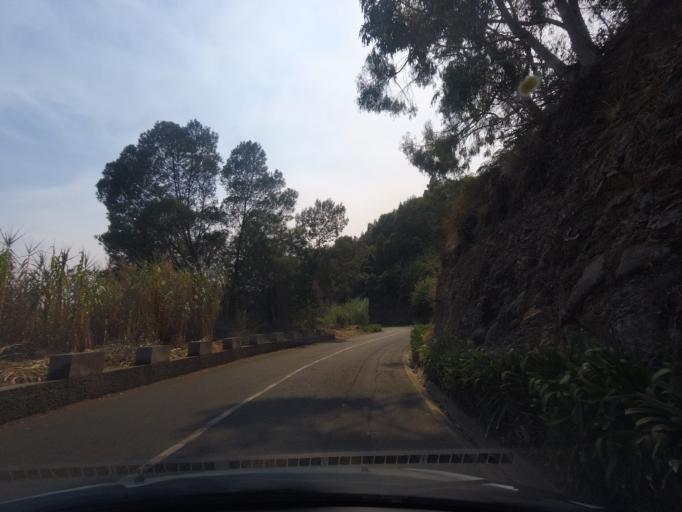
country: PT
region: Madeira
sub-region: Ribeira Brava
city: Campanario
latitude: 32.6909
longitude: -17.0604
